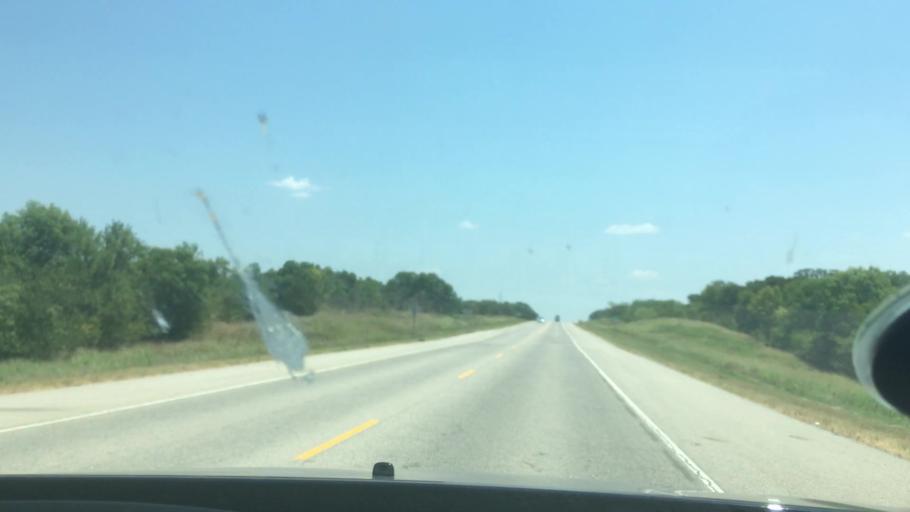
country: US
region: Oklahoma
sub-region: Pontotoc County
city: Ada
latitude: 34.6423
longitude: -96.5134
